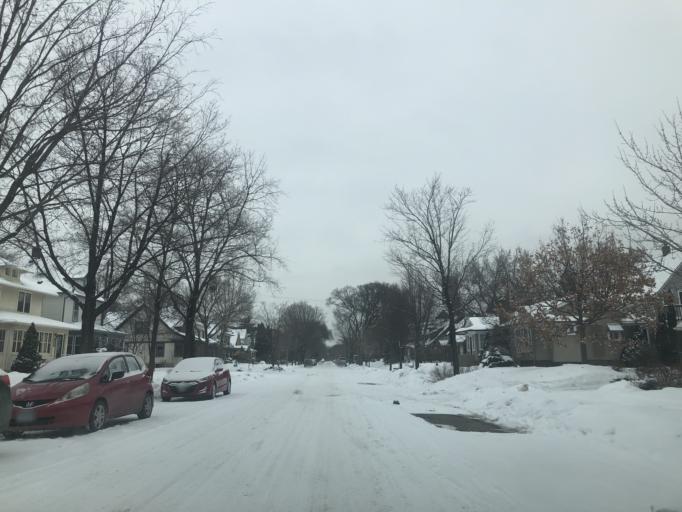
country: US
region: Minnesota
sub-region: Hennepin County
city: Richfield
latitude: 44.9317
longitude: -93.2831
